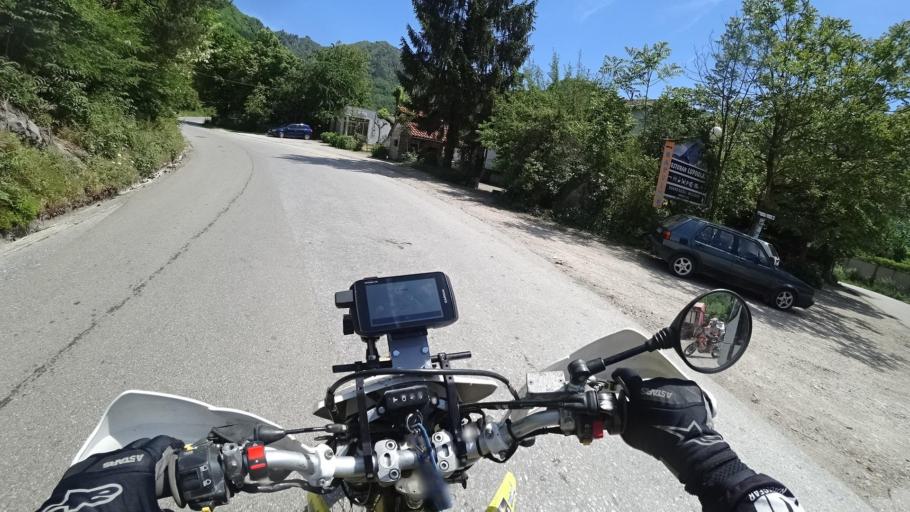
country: BA
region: Federation of Bosnia and Herzegovina
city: Polje-Bijela
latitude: 43.6250
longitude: 17.9677
